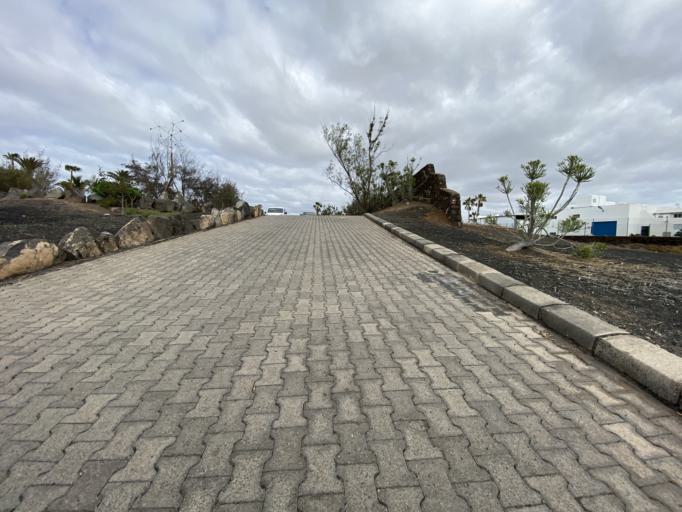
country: ES
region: Canary Islands
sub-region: Provincia de Las Palmas
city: Playa Blanca
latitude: 28.8612
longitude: -13.8468
